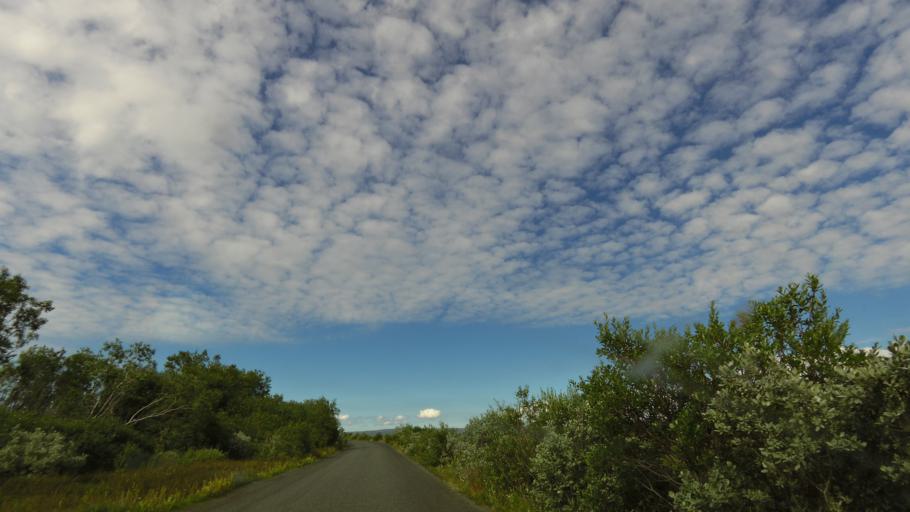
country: IS
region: Northeast
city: Husavik
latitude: 66.0235
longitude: -16.4947
